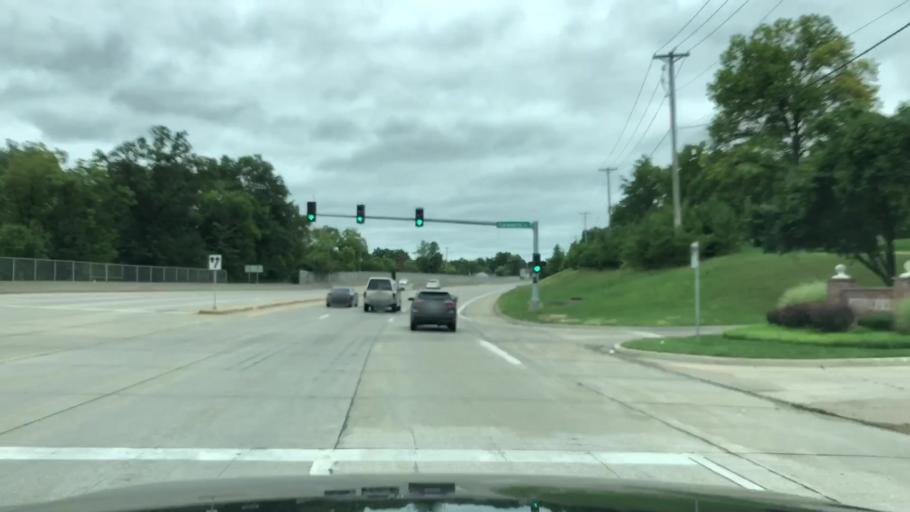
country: US
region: Missouri
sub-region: Saint Louis County
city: Manchester
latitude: 38.6088
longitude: -90.5111
